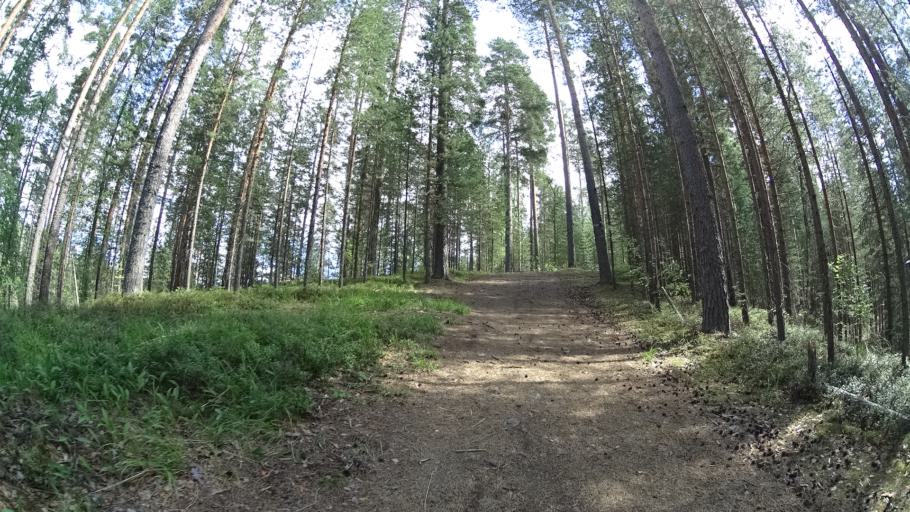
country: FI
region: Southern Savonia
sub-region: Savonlinna
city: Punkaharju
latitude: 61.7910
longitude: 29.3065
